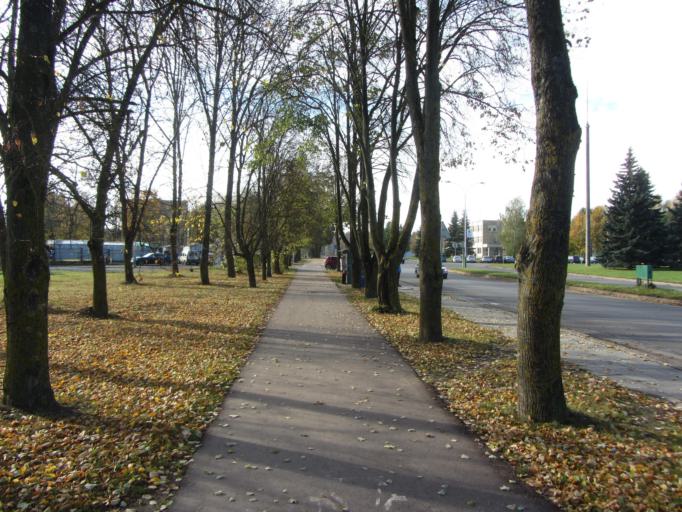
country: LT
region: Vilnius County
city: Elektrenai
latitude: 54.7851
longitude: 24.6565
